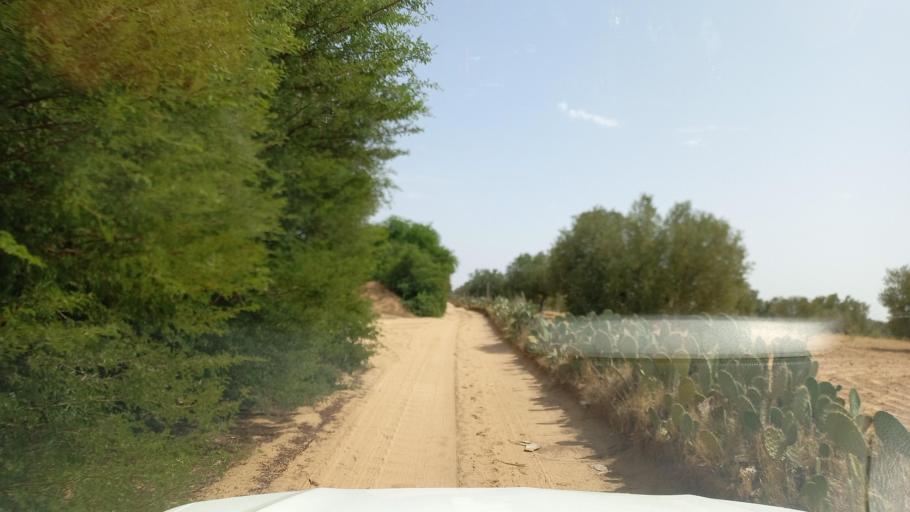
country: TN
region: Al Qasrayn
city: Kasserine
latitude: 35.2574
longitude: 9.0538
